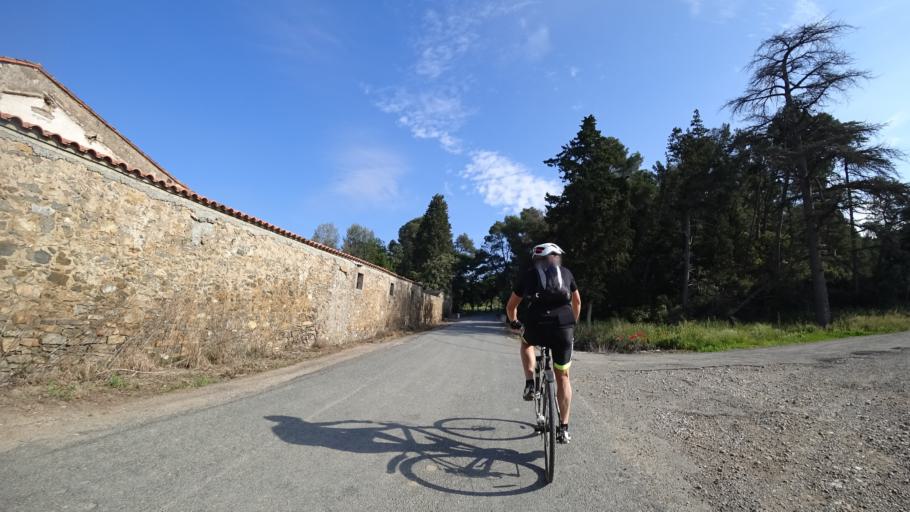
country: FR
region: Languedoc-Roussillon
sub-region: Departement de l'Herault
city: Olonzac
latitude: 43.2435
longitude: 2.7192
